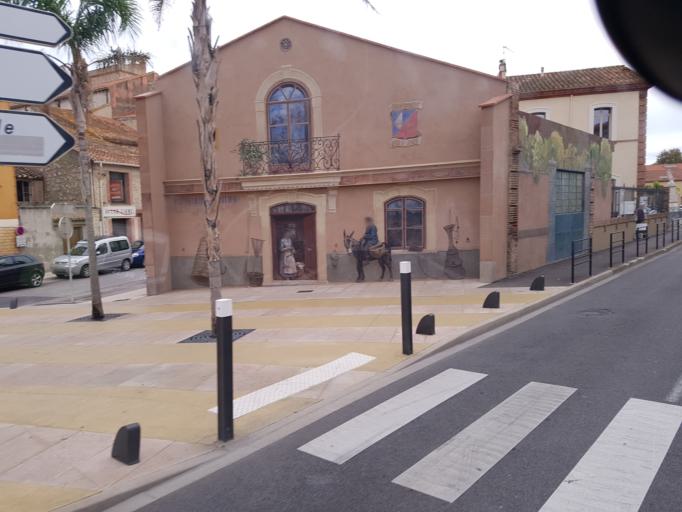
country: FR
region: Languedoc-Roussillon
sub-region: Departement des Pyrenees-Orientales
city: Saint-Laurent-de-la-Salanque
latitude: 42.7737
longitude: 2.9882
